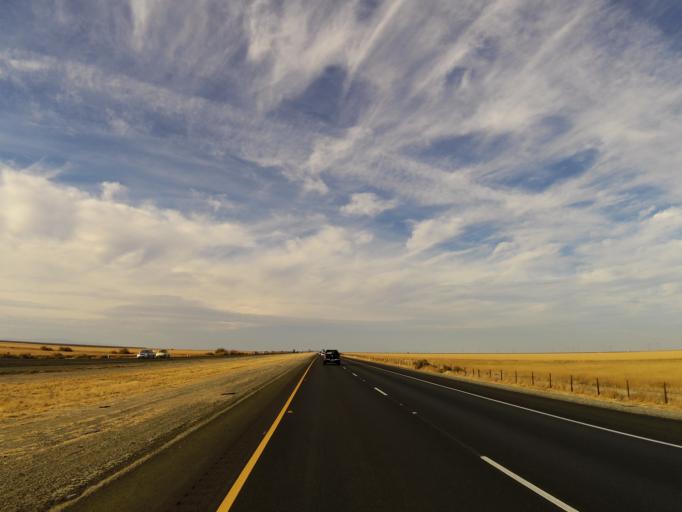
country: US
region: California
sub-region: Kern County
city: Lost Hills
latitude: 35.6438
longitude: -119.6736
